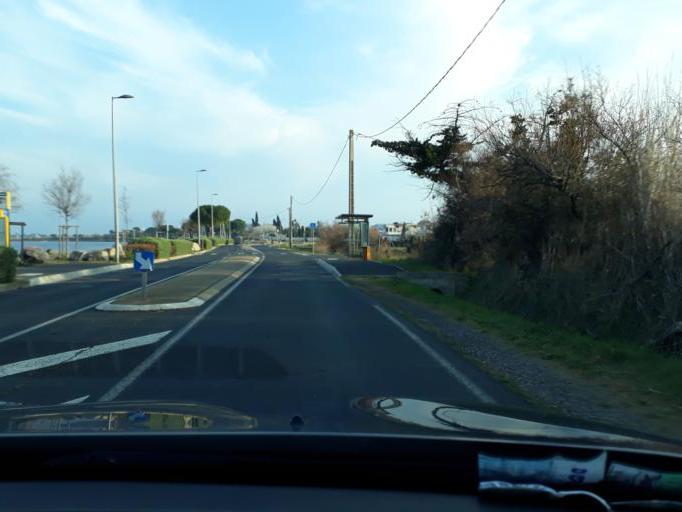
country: FR
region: Languedoc-Roussillon
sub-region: Departement de l'Herault
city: Marseillan
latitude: 43.3435
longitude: 3.5321
